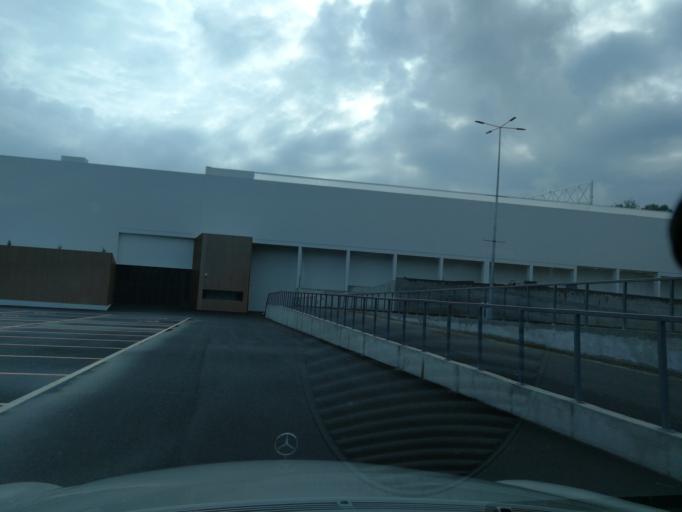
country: PT
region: Braga
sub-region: Braga
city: Braga
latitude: 41.5407
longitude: -8.4236
